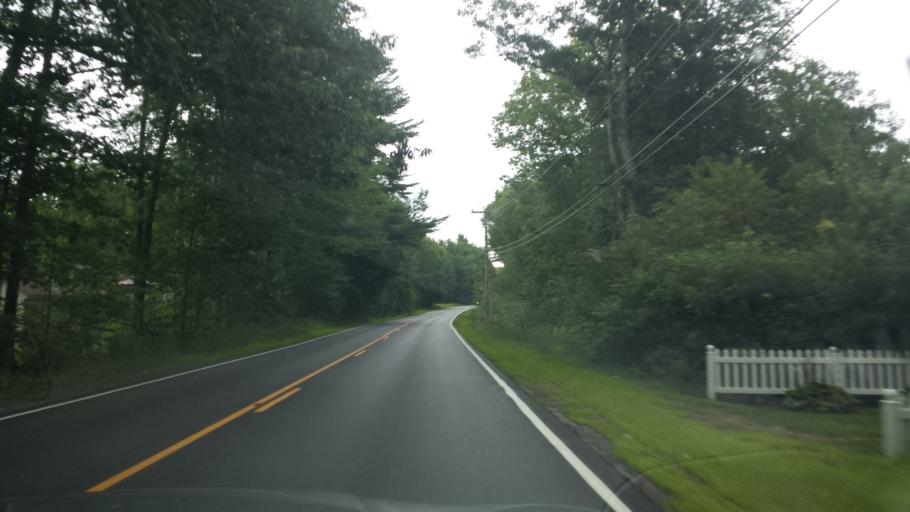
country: US
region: Maine
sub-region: York County
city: South Sanford
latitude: 43.4001
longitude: -70.6836
